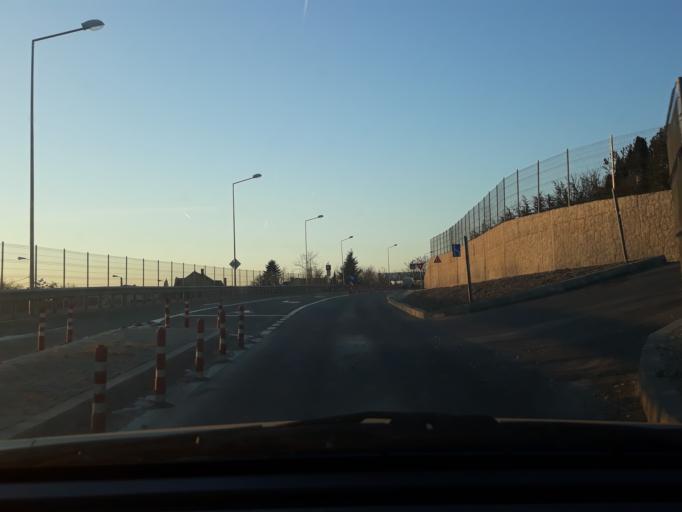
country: RO
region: Bihor
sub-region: Comuna Biharea
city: Oradea
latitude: 47.0556
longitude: 21.9503
